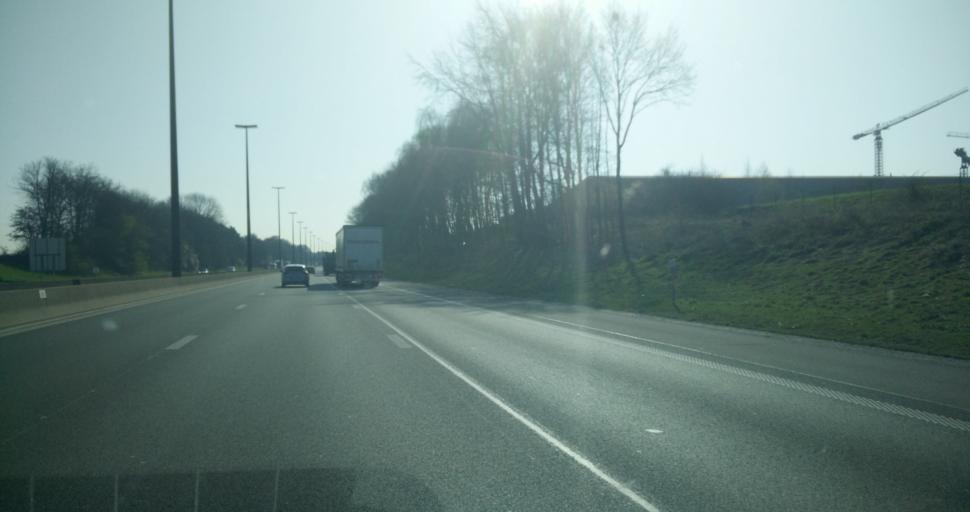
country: BE
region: Wallonia
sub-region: Province du Hainaut
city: Brunehault
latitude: 50.4793
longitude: 4.4669
